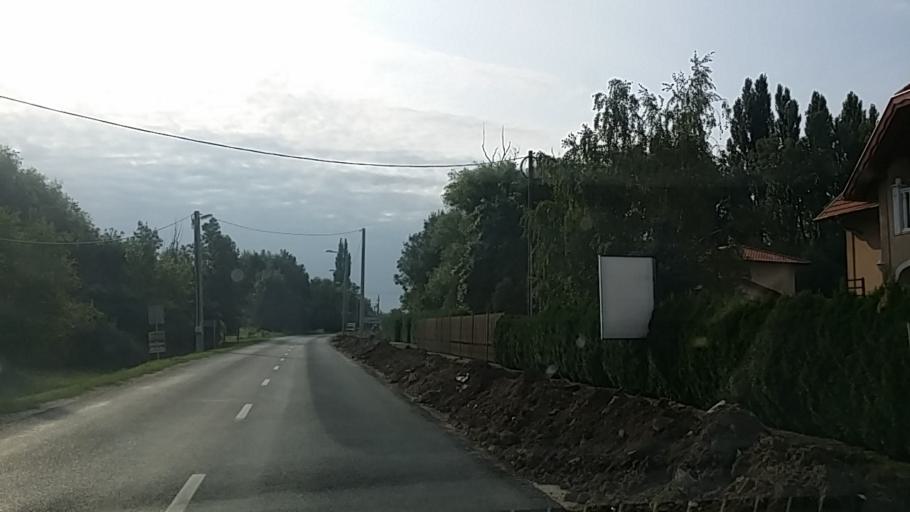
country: HU
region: Gyor-Moson-Sopron
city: Fertoszentmiklos
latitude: 47.6020
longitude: 16.9106
